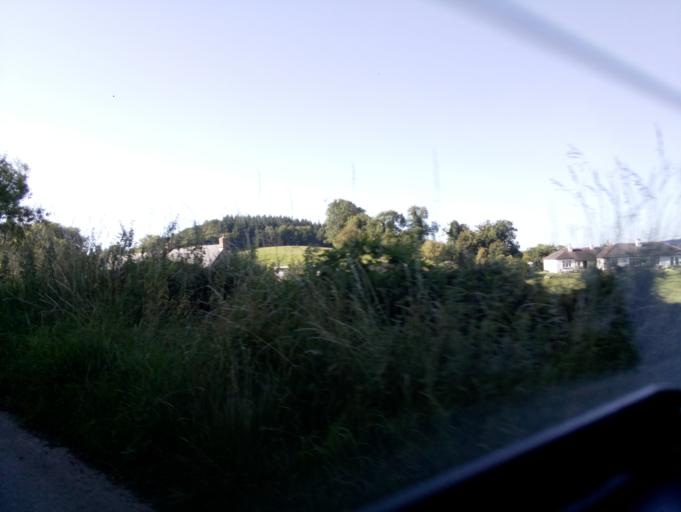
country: GB
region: England
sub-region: Gloucestershire
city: Coleford
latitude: 51.7917
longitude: -2.6402
